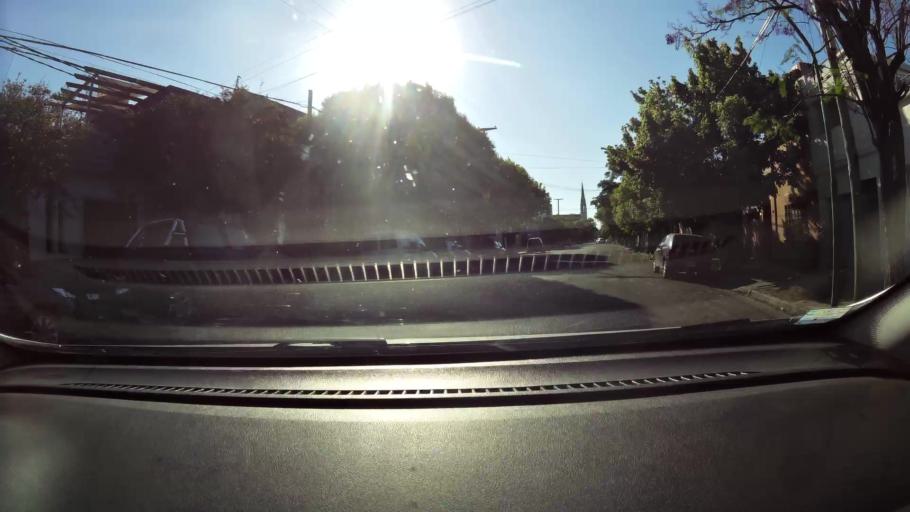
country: AR
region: Cordoba
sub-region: Departamento de Capital
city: Cordoba
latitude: -31.3959
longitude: -64.1774
